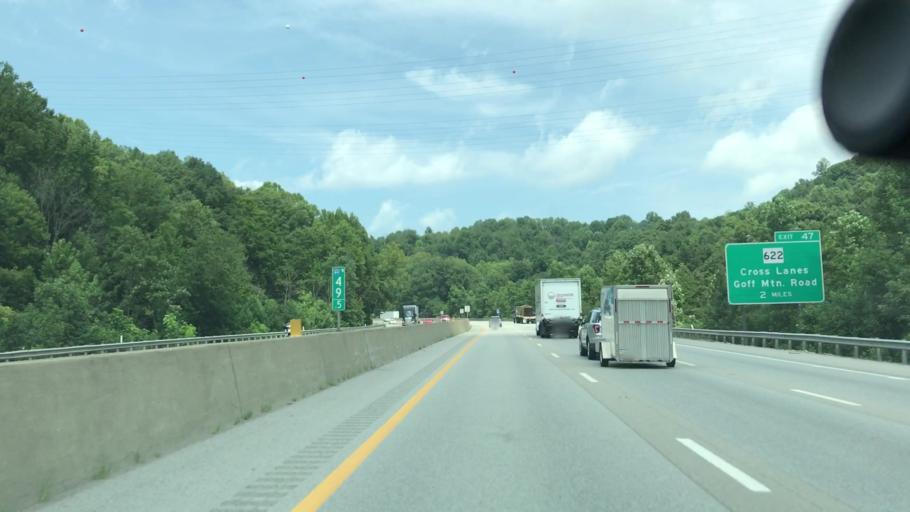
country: US
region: West Virginia
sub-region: Kanawha County
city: Cross Lanes
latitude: 38.3931
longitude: -81.7698
